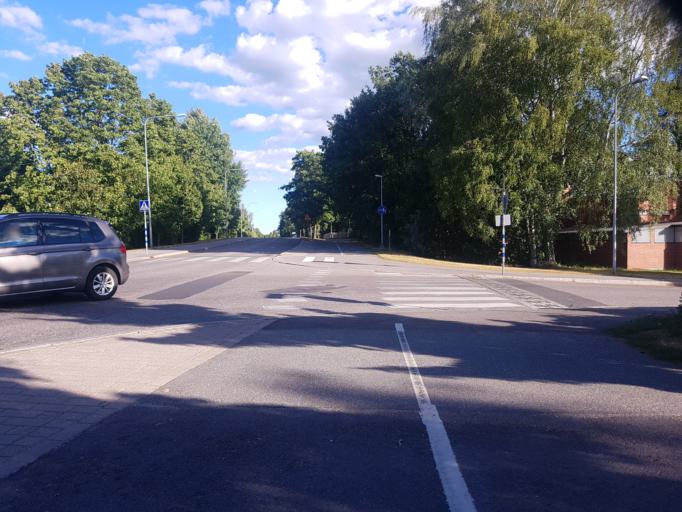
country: FI
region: Uusimaa
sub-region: Helsinki
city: Vantaa
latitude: 60.2620
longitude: 24.9850
